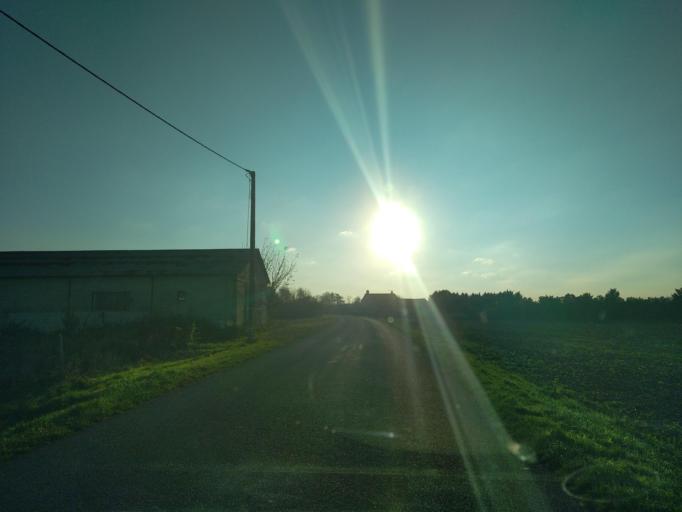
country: FR
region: Pays de la Loire
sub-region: Departement de la Vendee
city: Maillezais
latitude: 46.3368
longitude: -0.7776
